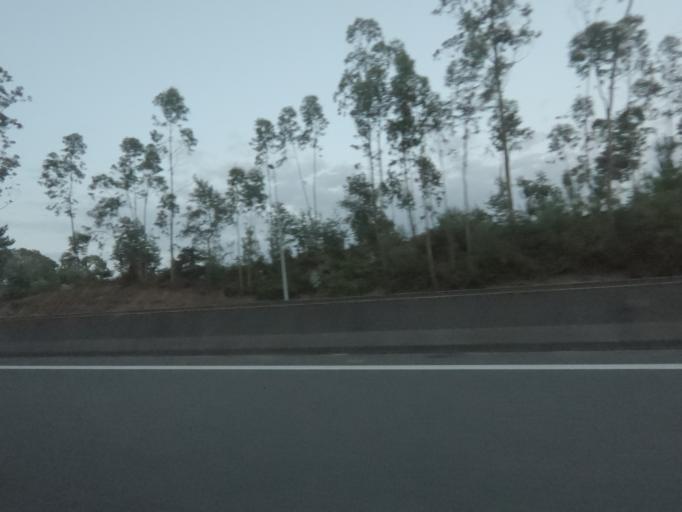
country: ES
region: Galicia
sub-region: Provincia de Pontevedra
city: Tui
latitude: 42.0699
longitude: -8.6329
